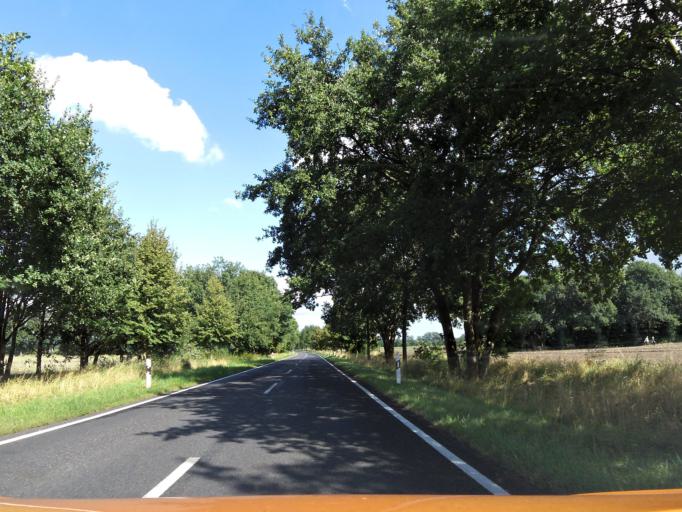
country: DE
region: Brandenburg
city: Ketzin
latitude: 52.4658
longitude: 12.9186
